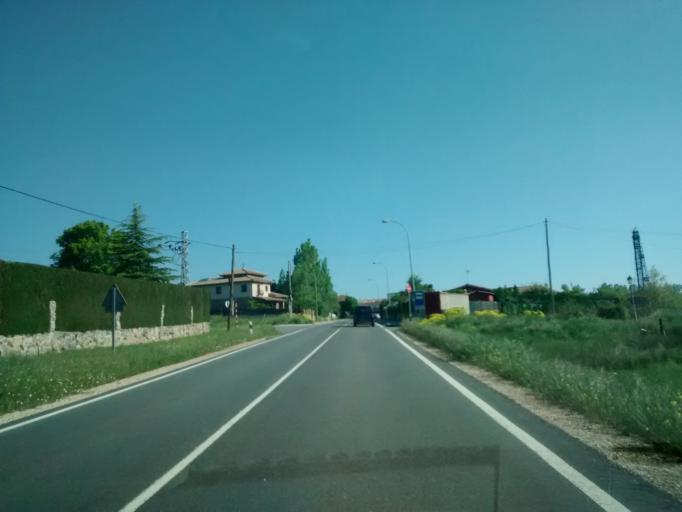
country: ES
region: Castille and Leon
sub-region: Provincia de Segovia
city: Torrecaballeros
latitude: 40.9892
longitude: -4.0236
